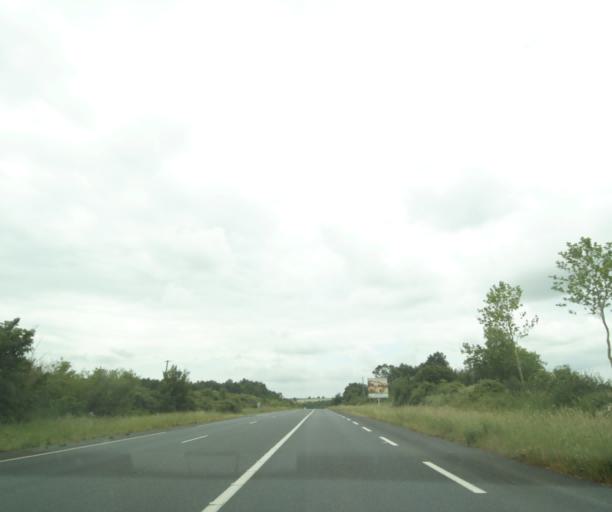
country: FR
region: Poitou-Charentes
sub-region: Departement des Deux-Sevres
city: Saint-Varent
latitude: 46.9077
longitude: -0.1921
